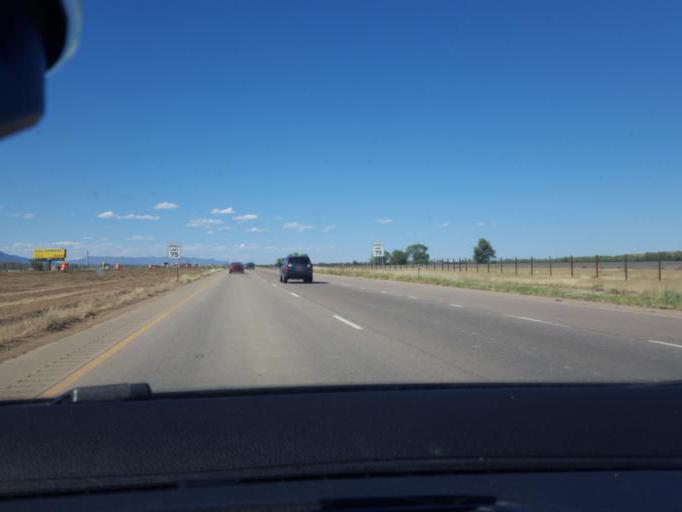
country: US
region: Colorado
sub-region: El Paso County
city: Fountain
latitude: 38.5939
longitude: -104.6729
